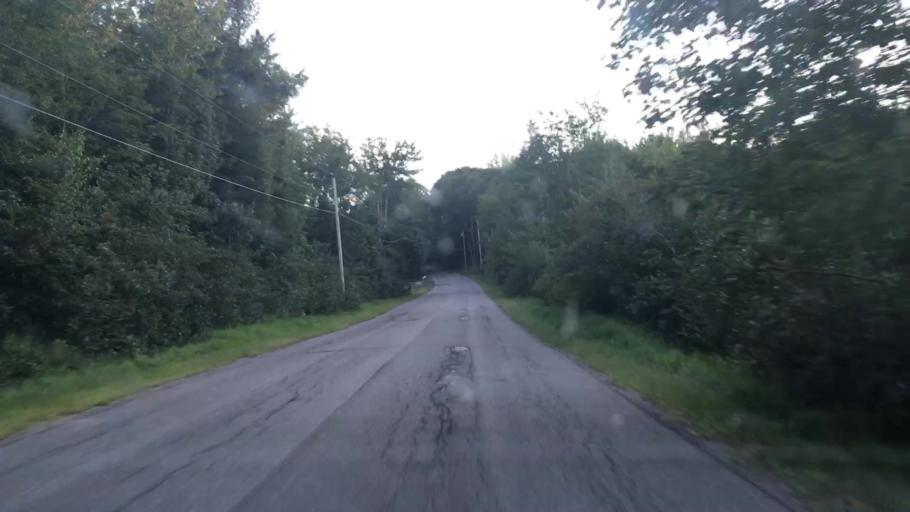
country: US
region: Maine
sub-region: Waldo County
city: Frankfort
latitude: 44.6605
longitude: -68.9322
